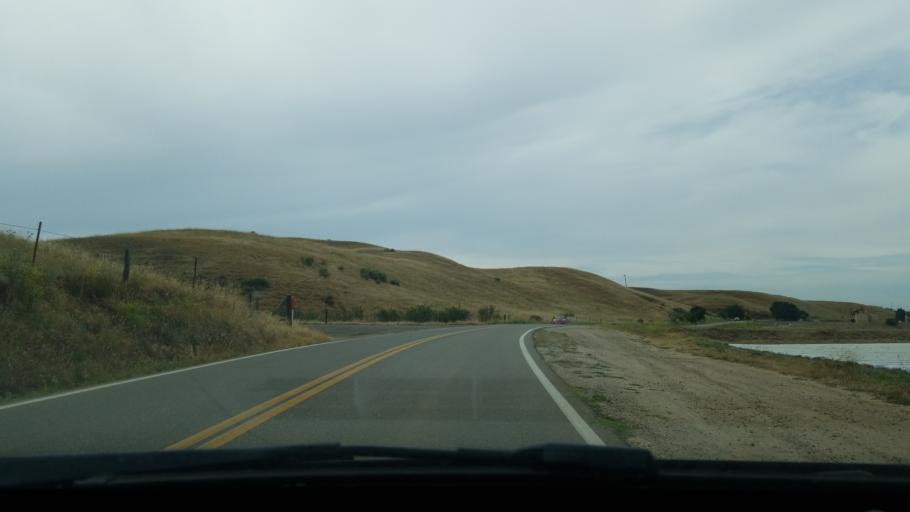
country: US
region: California
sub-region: Santa Barbara County
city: Orcutt
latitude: 34.8732
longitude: -120.3067
